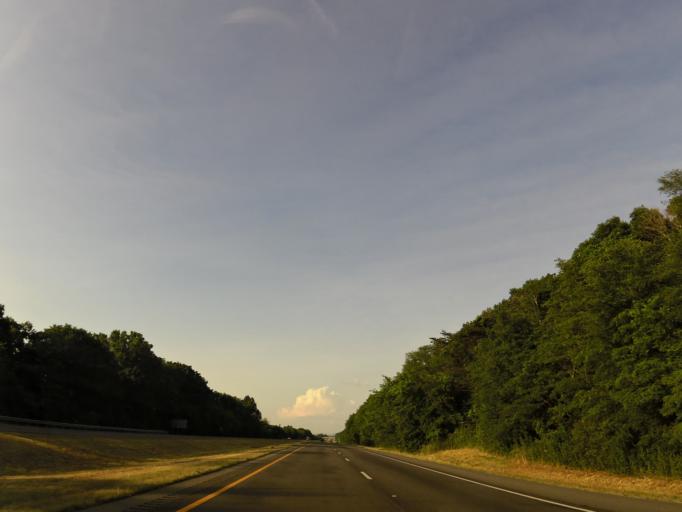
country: US
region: Alabama
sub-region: DeKalb County
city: Fort Payne
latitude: 34.4576
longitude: -85.7294
